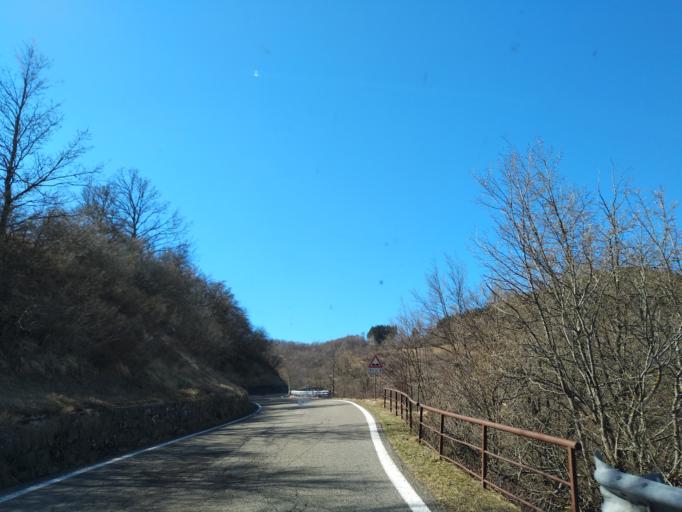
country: IT
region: Emilia-Romagna
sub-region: Provincia di Reggio Emilia
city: Ramiseto
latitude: 44.4060
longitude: 10.2684
